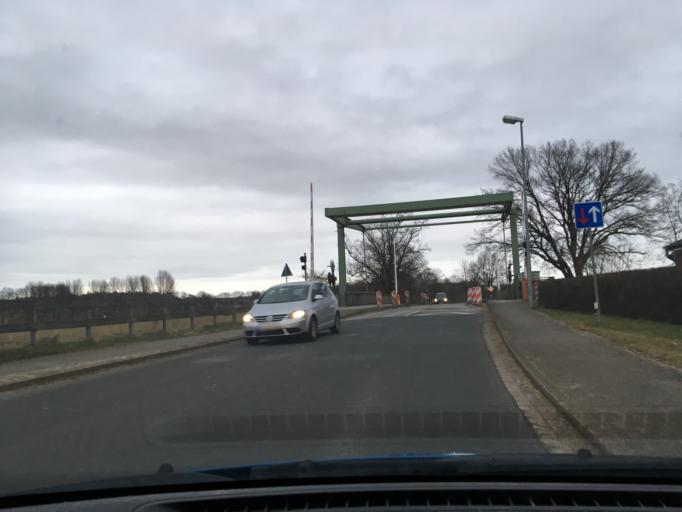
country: DE
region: Lower Saxony
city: Wittorf
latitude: 53.3323
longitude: 10.3838
